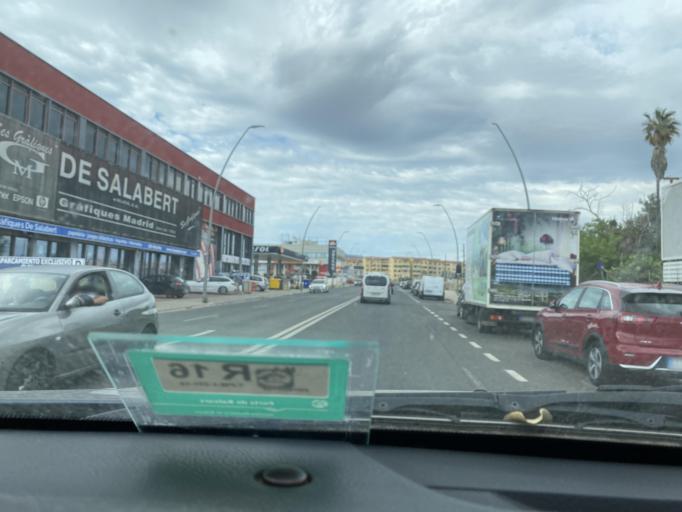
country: ES
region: Balearic Islands
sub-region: Illes Balears
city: Palma
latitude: 39.6015
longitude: 2.6744
